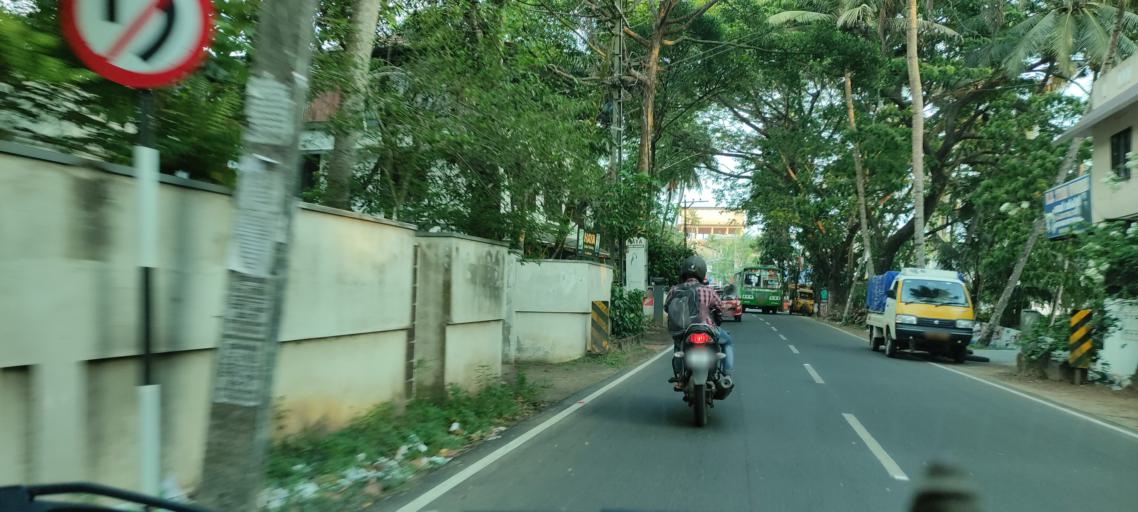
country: IN
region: Kerala
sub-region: Alappuzha
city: Arukutti
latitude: 9.8525
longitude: 76.3267
